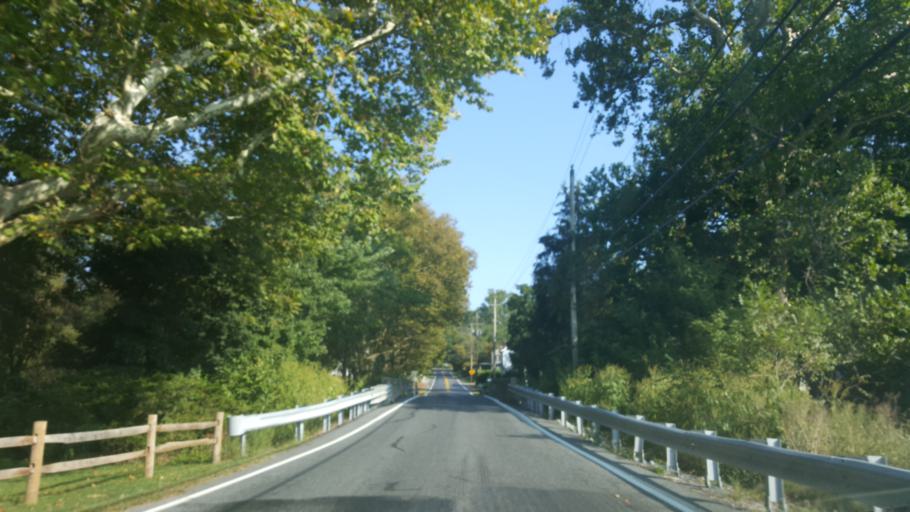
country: US
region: Pennsylvania
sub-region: Lebanon County
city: Campbelltown
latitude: 40.2224
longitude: -76.5417
